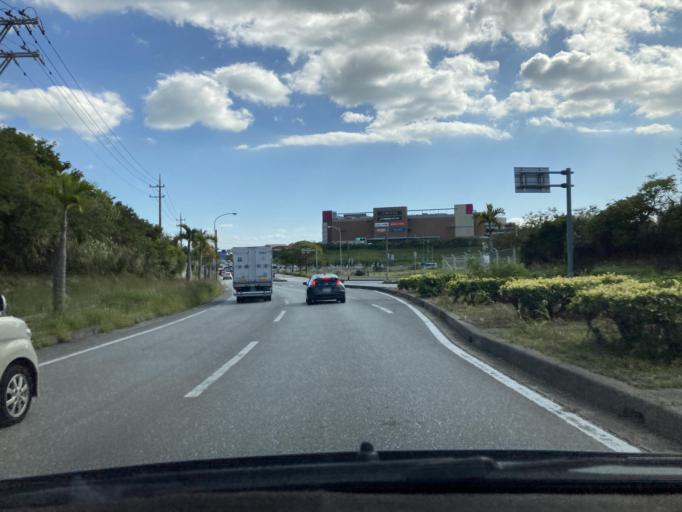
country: JP
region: Okinawa
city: Okinawa
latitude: 26.3170
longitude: 127.7911
